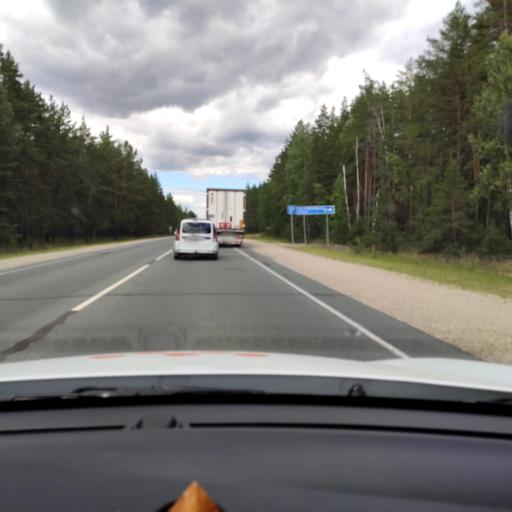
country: RU
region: Mariy-El
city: Krasnogorskiy
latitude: 56.1070
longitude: 48.3444
